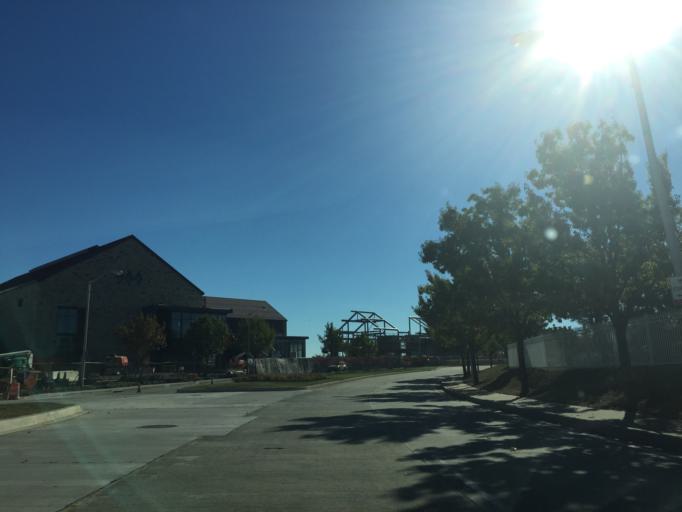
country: US
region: Maryland
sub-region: City of Baltimore
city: Baltimore
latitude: 39.2651
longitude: -76.6066
